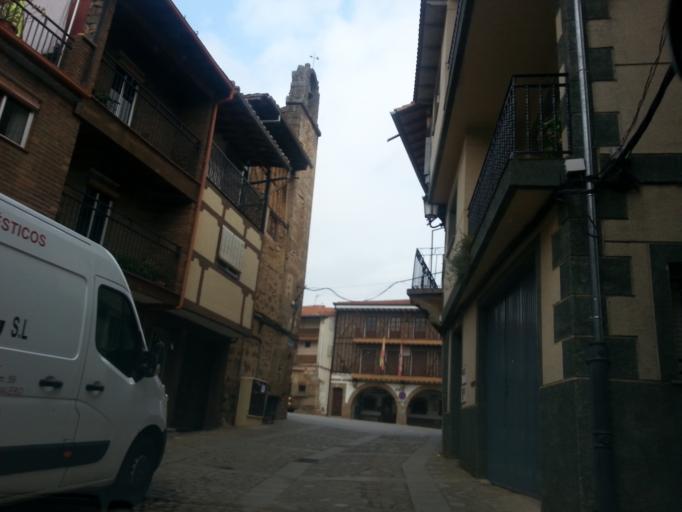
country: ES
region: Castille and Leon
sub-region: Provincia de Salamanca
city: Sotoserrano
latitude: 40.4370
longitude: -6.0332
